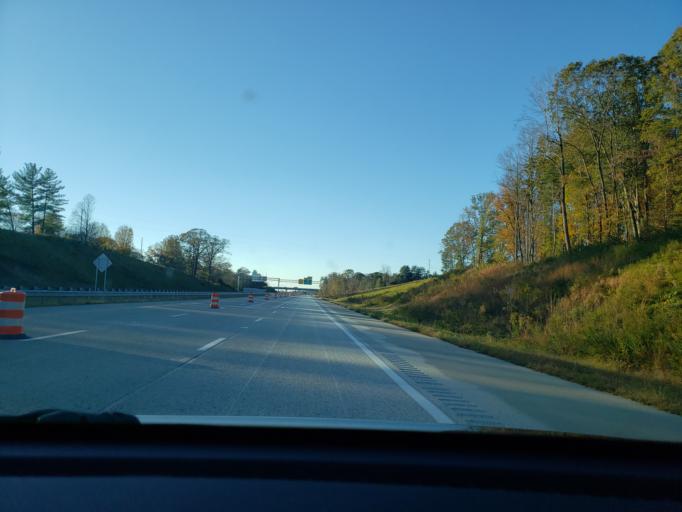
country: US
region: North Carolina
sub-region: Forsyth County
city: Walkertown
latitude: 36.1377
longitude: -80.1389
